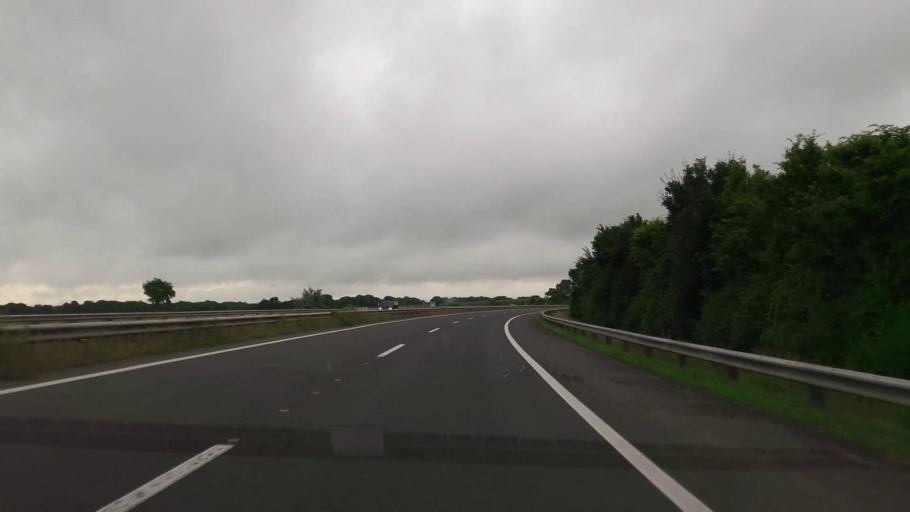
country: AT
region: Lower Austria
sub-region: Politischer Bezirk Modling
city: Munchendorf
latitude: 48.0051
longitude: 16.3814
